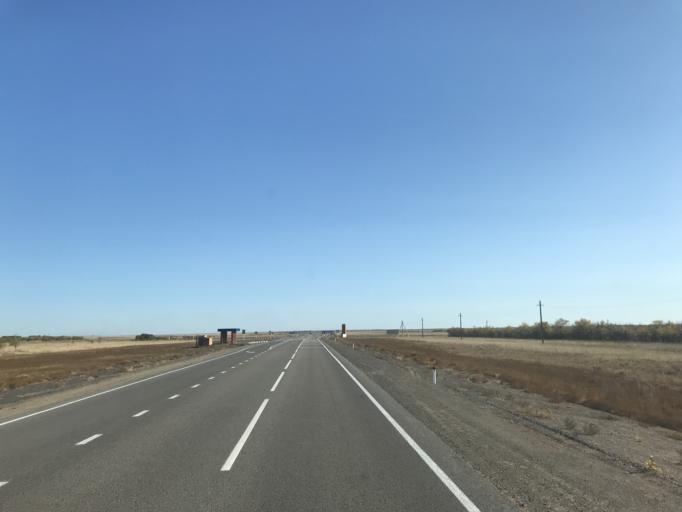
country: KZ
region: Pavlodar
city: Koktobe
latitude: 51.8995
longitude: 77.3879
